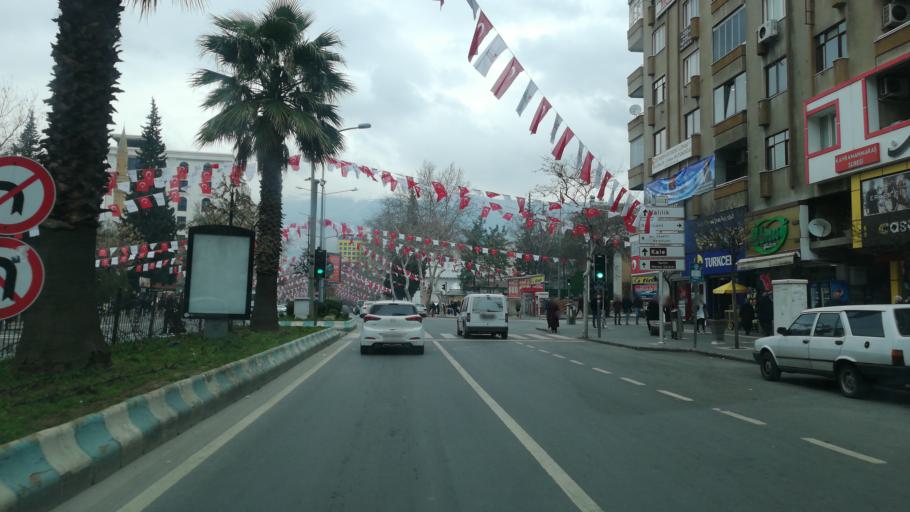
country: TR
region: Kahramanmaras
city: Kahramanmaras
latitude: 37.5766
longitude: 36.9318
